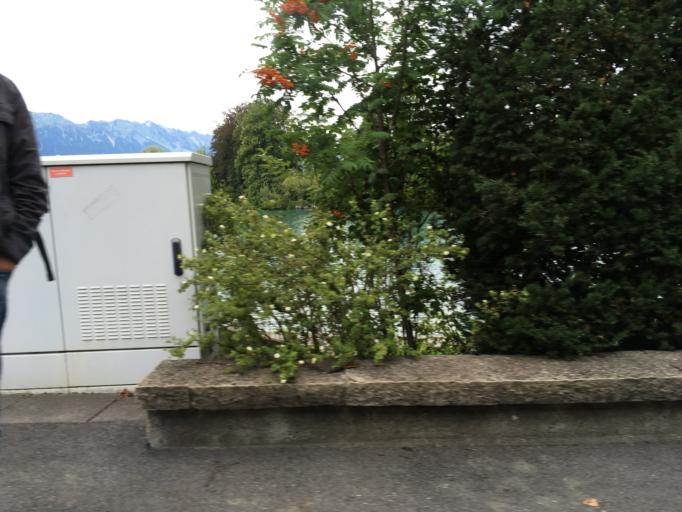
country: CH
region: Bern
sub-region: Thun District
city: Thun
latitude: 46.7517
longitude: 7.6370
